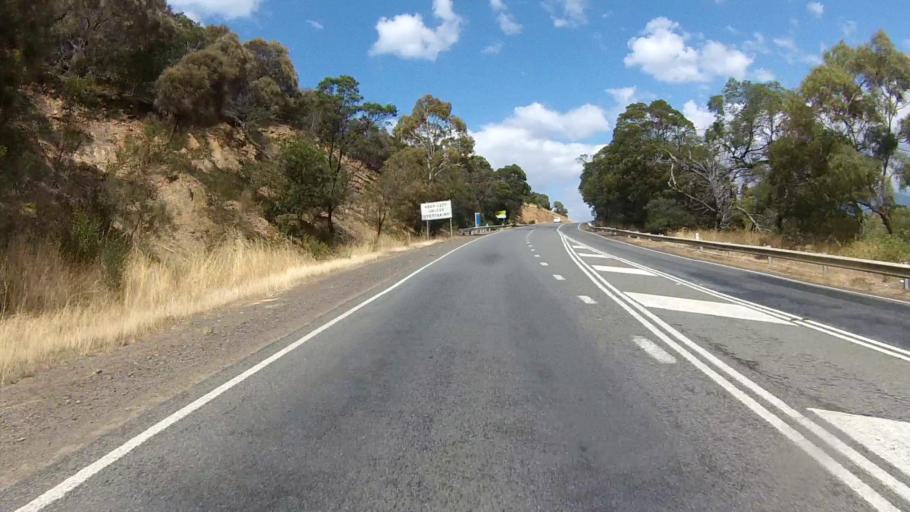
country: AU
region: Tasmania
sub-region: Brighton
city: Old Beach
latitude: -42.7901
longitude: 147.2931
